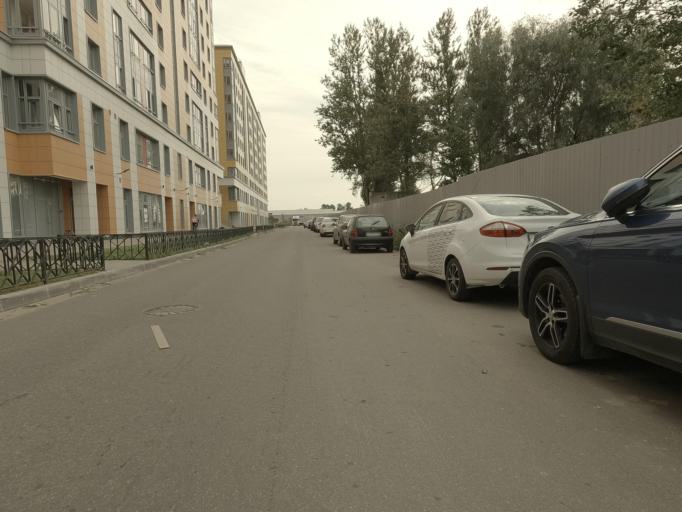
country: RU
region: St.-Petersburg
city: Admiralteisky
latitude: 59.8979
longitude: 30.3072
